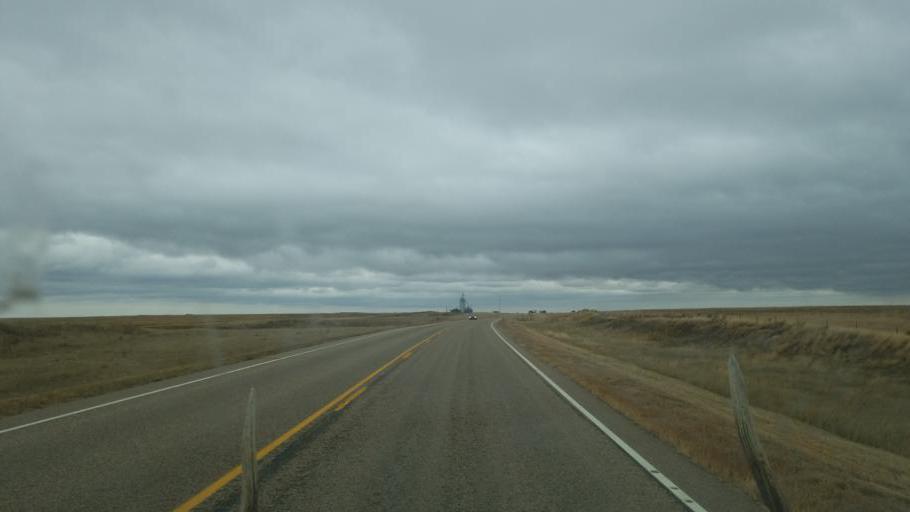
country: US
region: Colorado
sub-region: Cheyenne County
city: Cheyenne Wells
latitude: 38.8157
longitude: -102.5547
